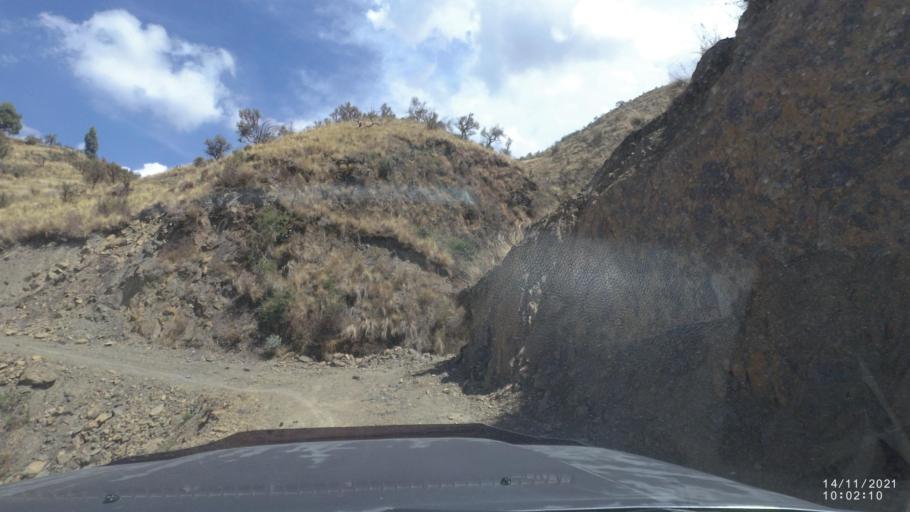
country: BO
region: Cochabamba
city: Cochabamba
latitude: -17.3505
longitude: -66.0903
